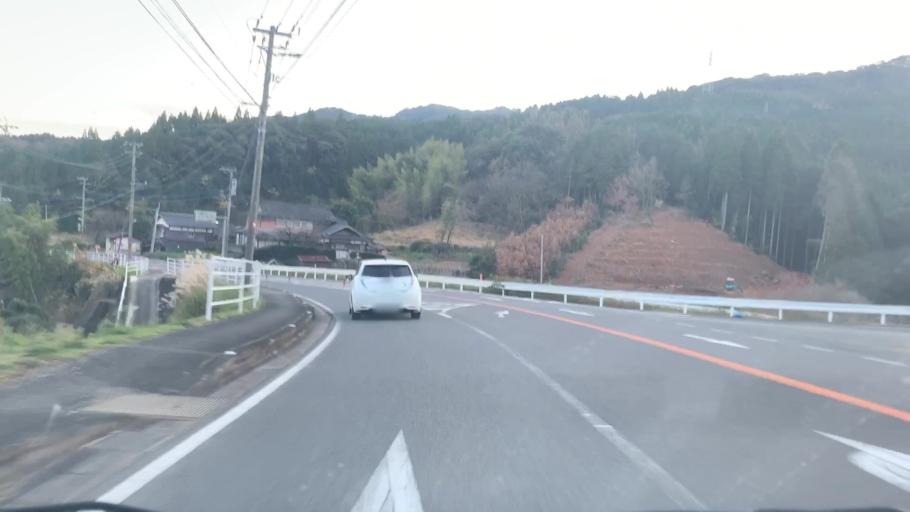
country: JP
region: Saga Prefecture
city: Takeocho-takeo
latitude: 33.2341
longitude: 130.0127
